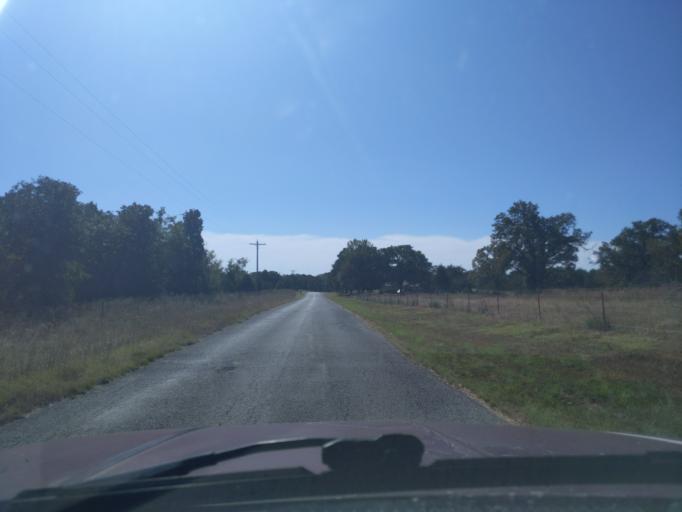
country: US
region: Oklahoma
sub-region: Creek County
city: Bristow
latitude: 35.6949
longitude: -96.4104
